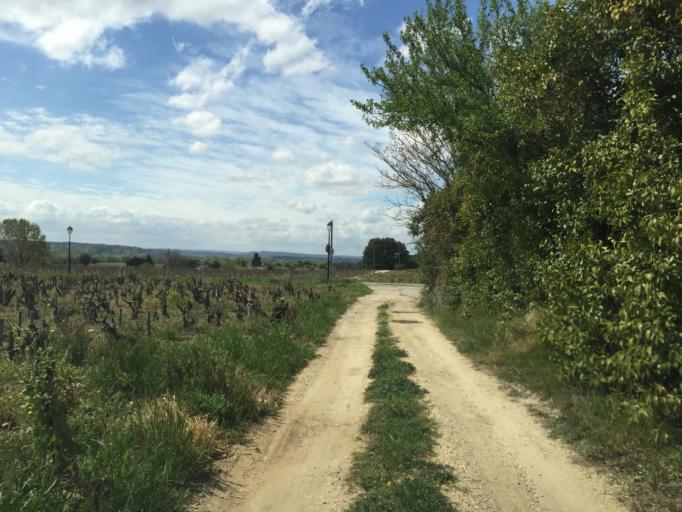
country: FR
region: Provence-Alpes-Cote d'Azur
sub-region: Departement du Vaucluse
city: Chateauneuf-du-Pape
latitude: 44.0526
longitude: 4.8320
